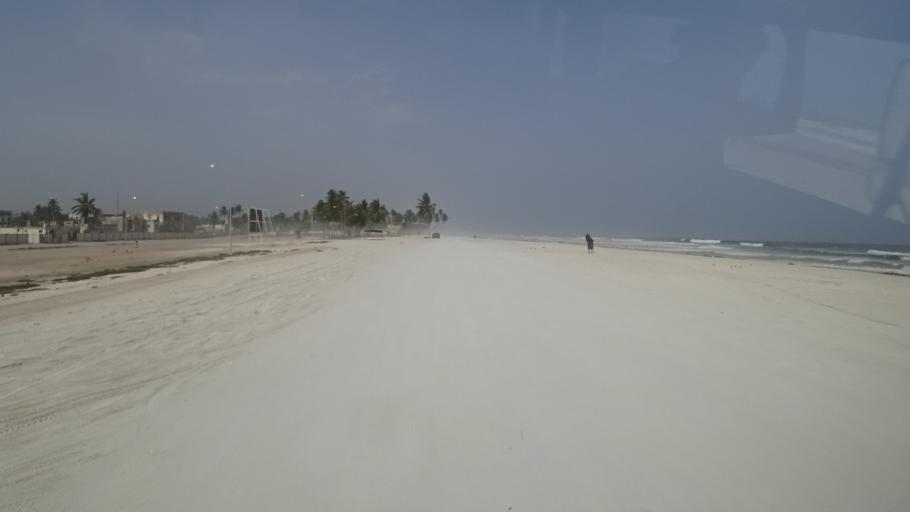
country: OM
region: Zufar
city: Salalah
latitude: 17.0005
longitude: 54.1073
